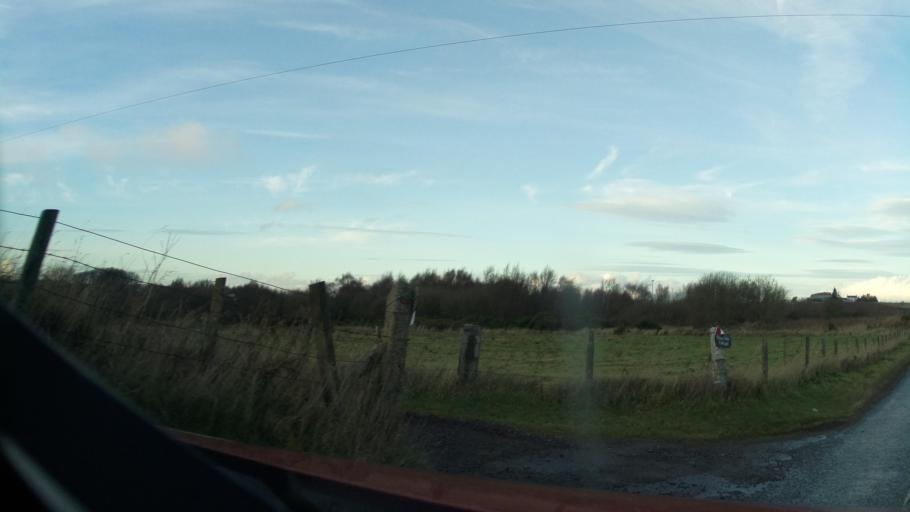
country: GB
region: Scotland
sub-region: Angus
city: Letham
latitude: 56.5758
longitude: -2.7800
